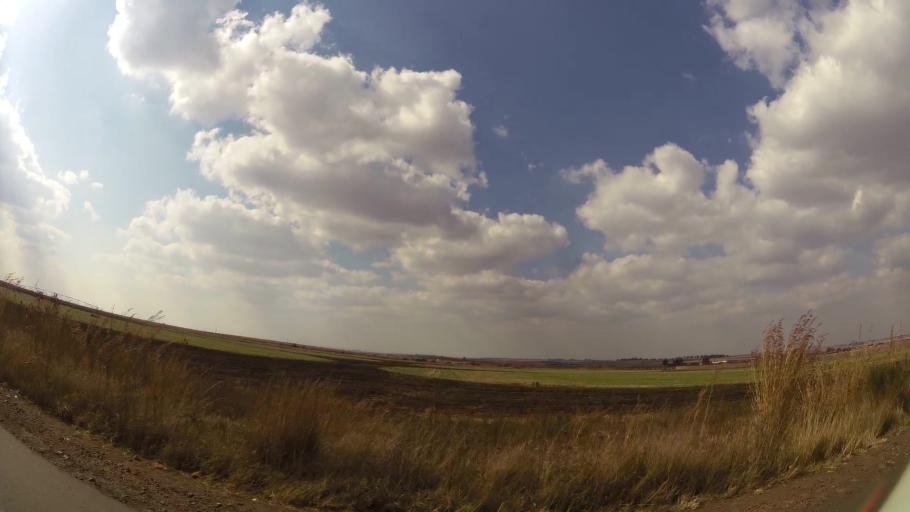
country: ZA
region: Mpumalanga
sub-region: Nkangala District Municipality
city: Delmas
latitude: -26.1218
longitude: 28.6828
